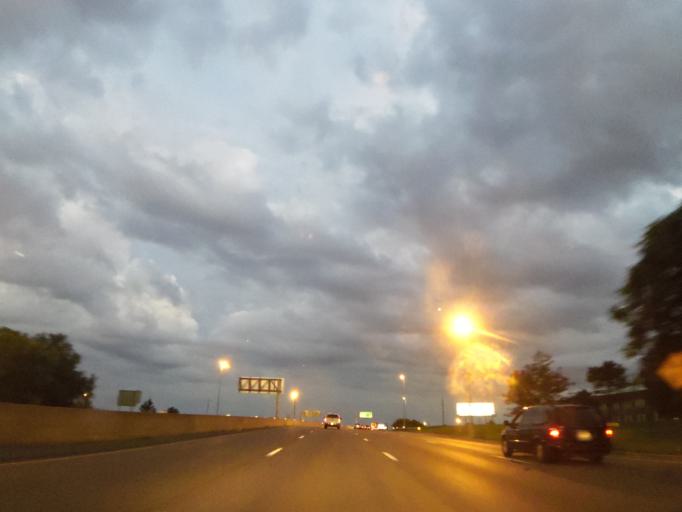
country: US
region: Illinois
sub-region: Saint Clair County
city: Cahokia
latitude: 38.5931
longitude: -90.2154
